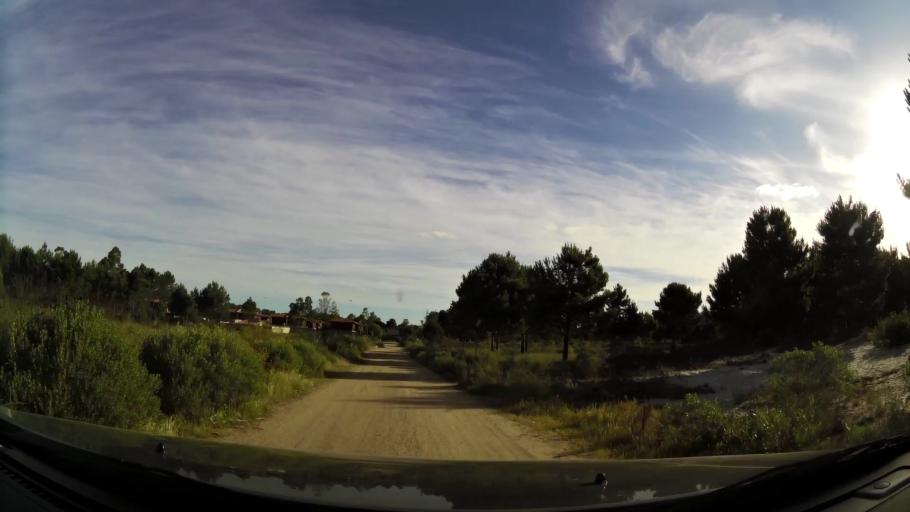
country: UY
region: Canelones
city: Empalme Olmos
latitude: -34.7648
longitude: -55.8581
